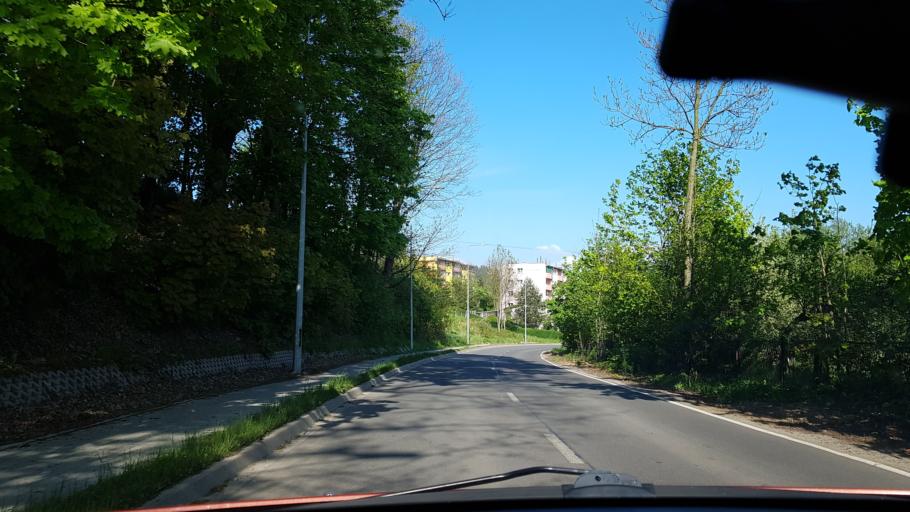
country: PL
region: Lower Silesian Voivodeship
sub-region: Powiat klodzki
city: Nowa Ruda
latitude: 50.5803
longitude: 16.4876
